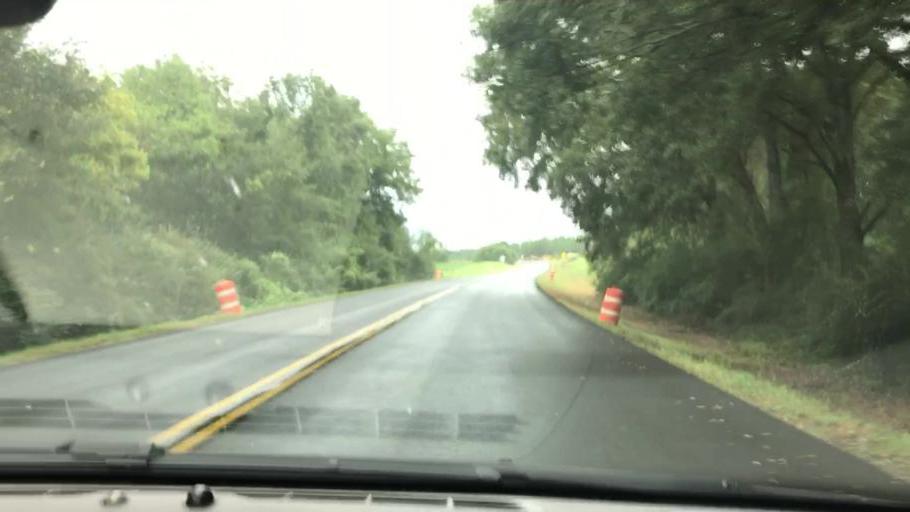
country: US
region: Georgia
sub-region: Early County
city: Blakely
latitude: 31.4073
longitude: -84.9613
